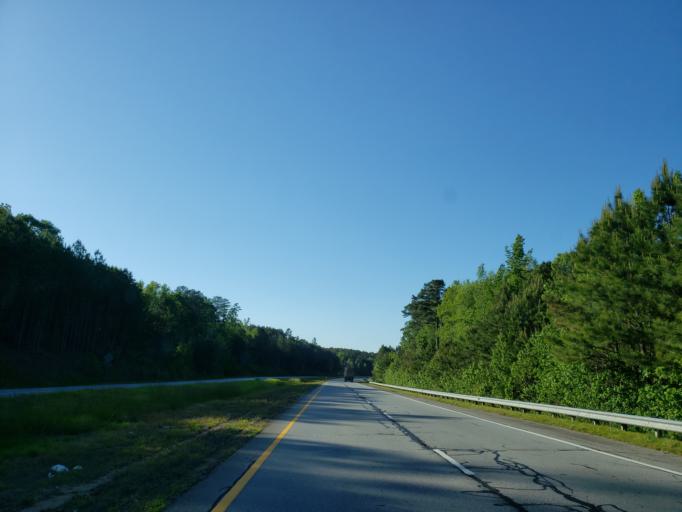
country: US
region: Georgia
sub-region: Haralson County
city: Buchanan
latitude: 33.8481
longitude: -85.2079
